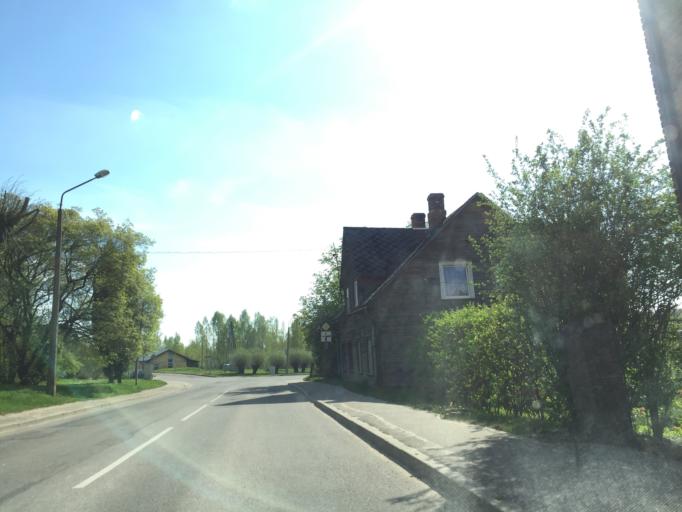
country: LV
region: Limbazu Rajons
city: Limbazi
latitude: 57.5107
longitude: 24.7063
